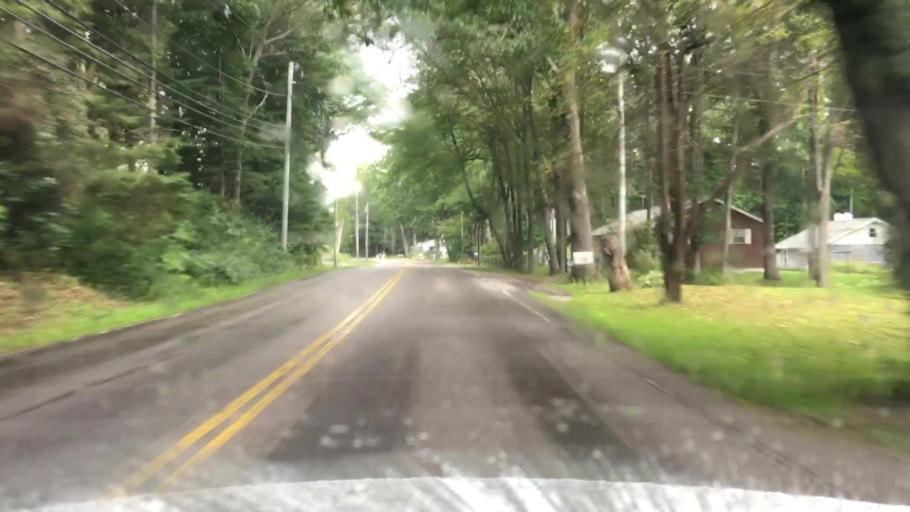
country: US
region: Maine
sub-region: York County
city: Wells Beach Station
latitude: 43.2954
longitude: -70.5938
